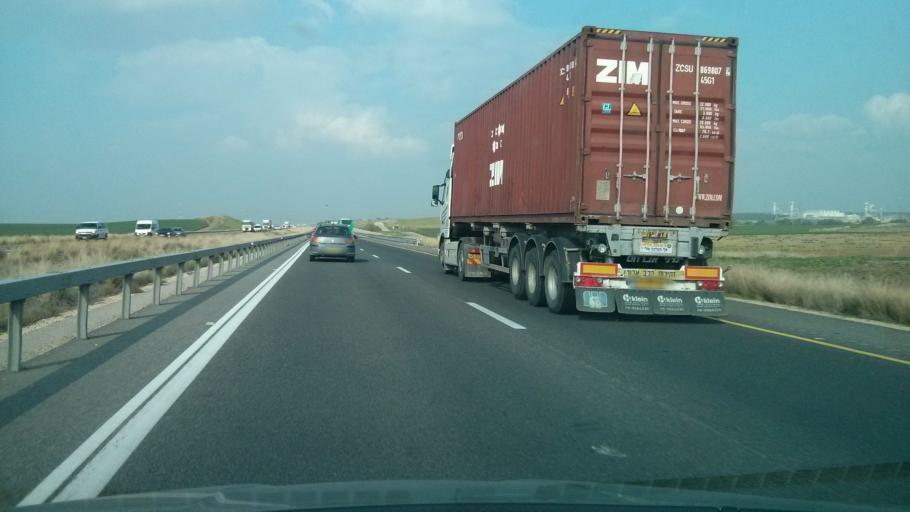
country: IL
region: Southern District
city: Qiryat Gat
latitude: 31.6983
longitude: 34.8162
